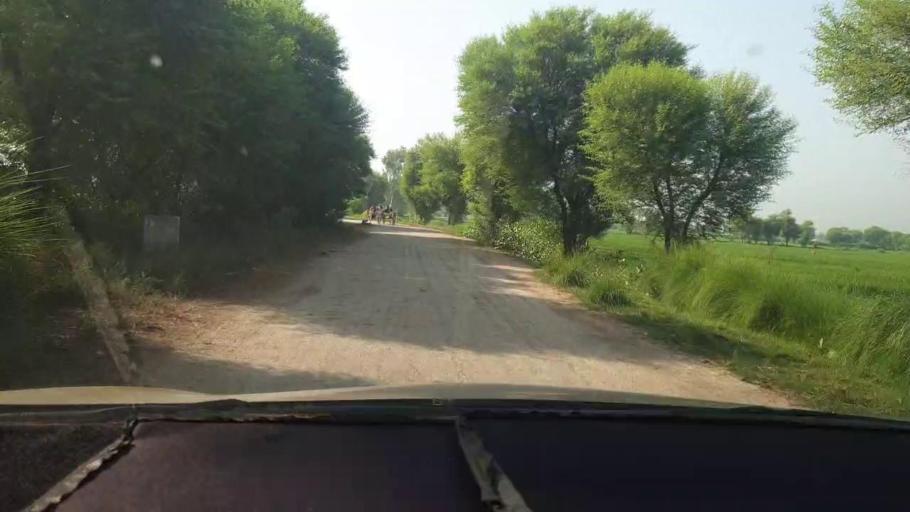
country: PK
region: Sindh
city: Kambar
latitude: 27.6157
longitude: 68.0908
